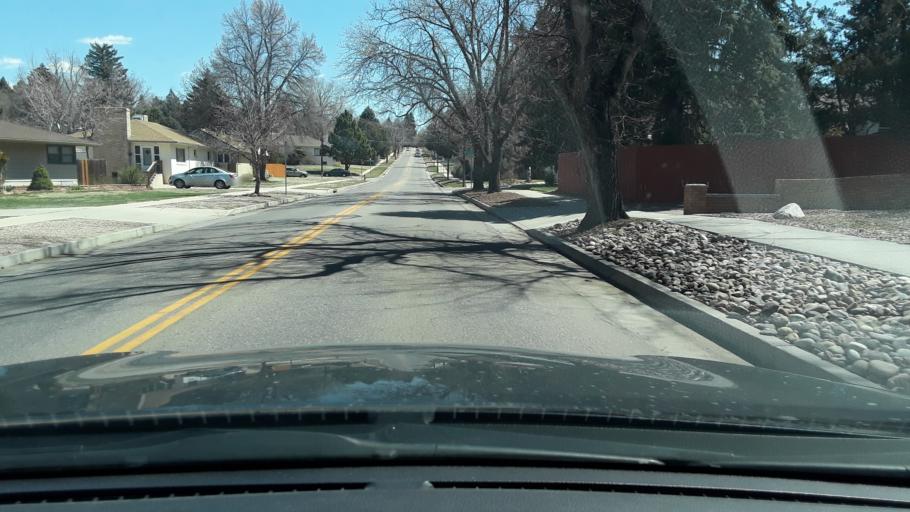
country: US
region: Colorado
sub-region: El Paso County
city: Colorado Springs
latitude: 38.8499
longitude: -104.7996
